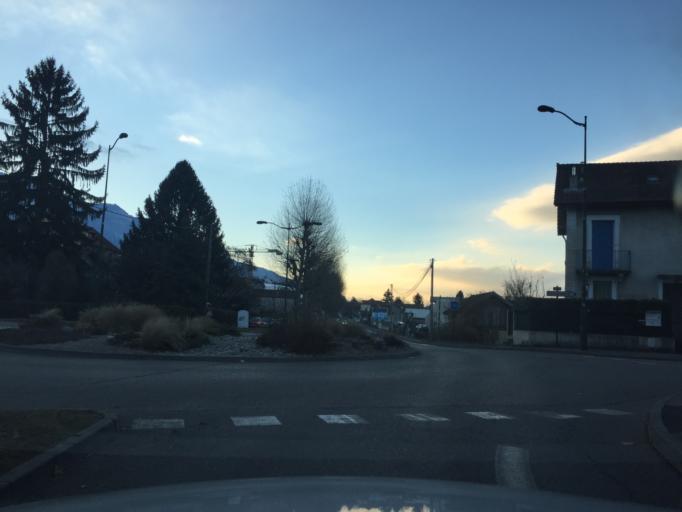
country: FR
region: Rhone-Alpes
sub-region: Departement de la Savoie
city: Tresserve
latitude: 45.6857
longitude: 5.9058
